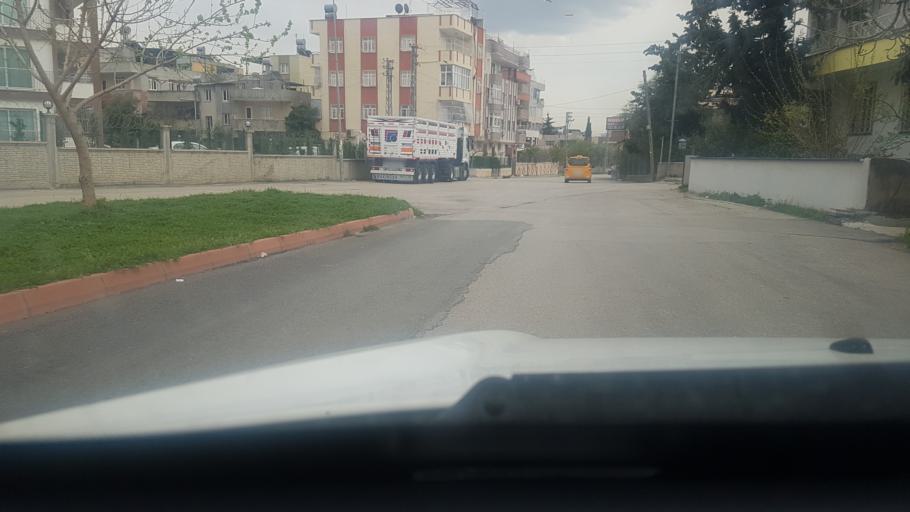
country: TR
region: Adana
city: Seyhan
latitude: 37.0196
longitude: 35.2763
